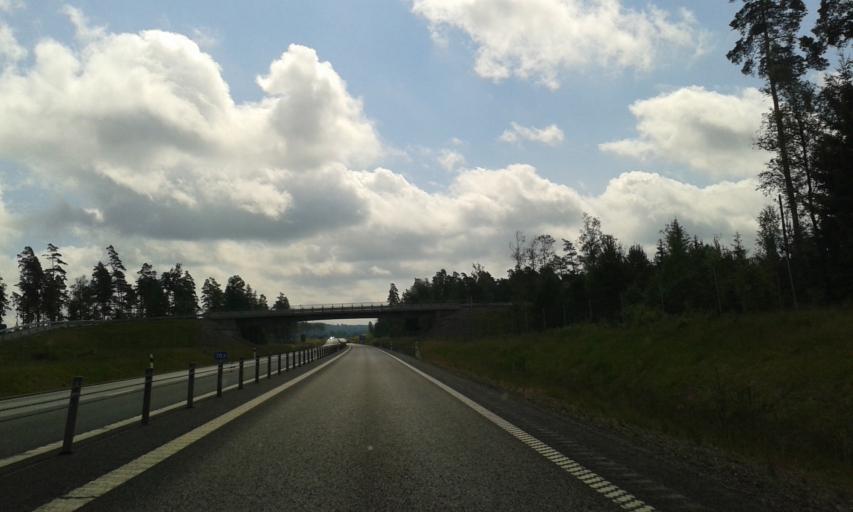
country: SE
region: Joenkoeping
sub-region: Gislaveds Kommun
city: Gislaved
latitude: 57.2909
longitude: 13.5952
